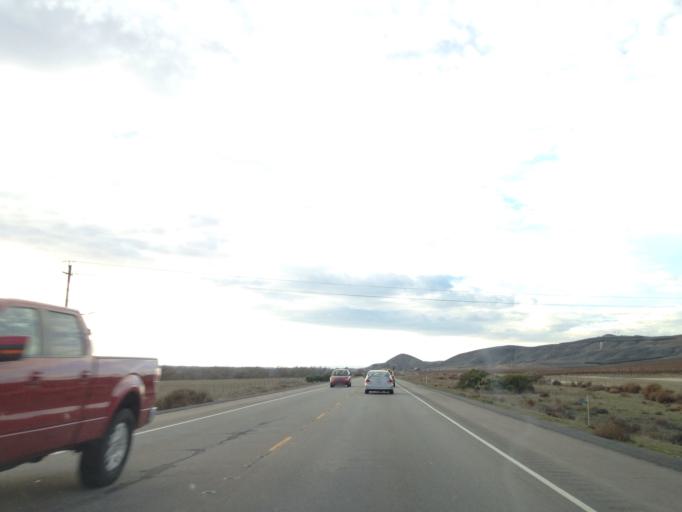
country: US
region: California
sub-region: San Luis Obispo County
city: Shandon
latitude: 35.6625
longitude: -120.3789
